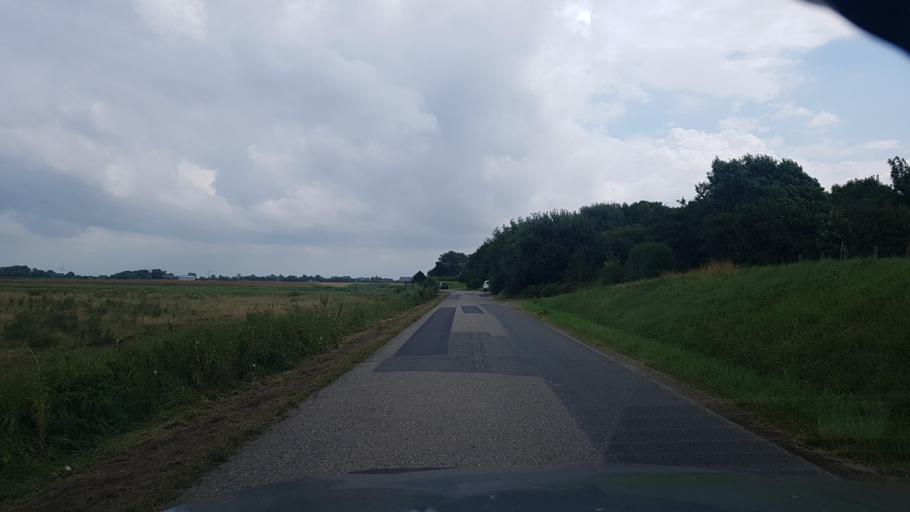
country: DE
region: Schleswig-Holstein
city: Elisabeth-Sophien-Koog
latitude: 54.4824
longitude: 8.8293
